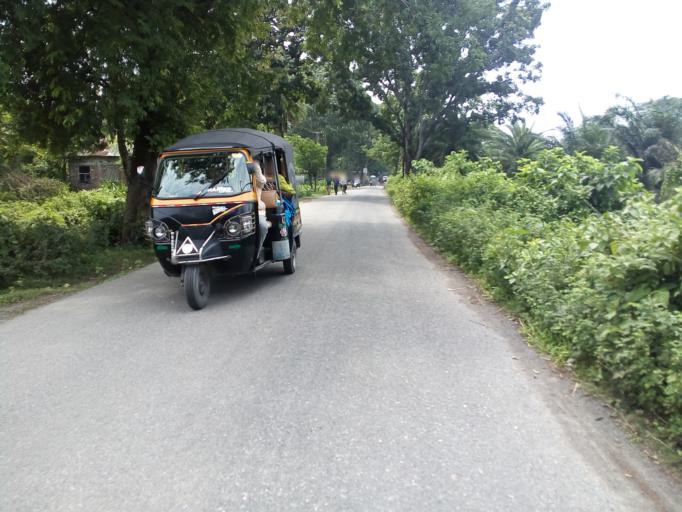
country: BD
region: Dhaka
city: Faridpur
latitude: 23.5531
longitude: 89.6265
